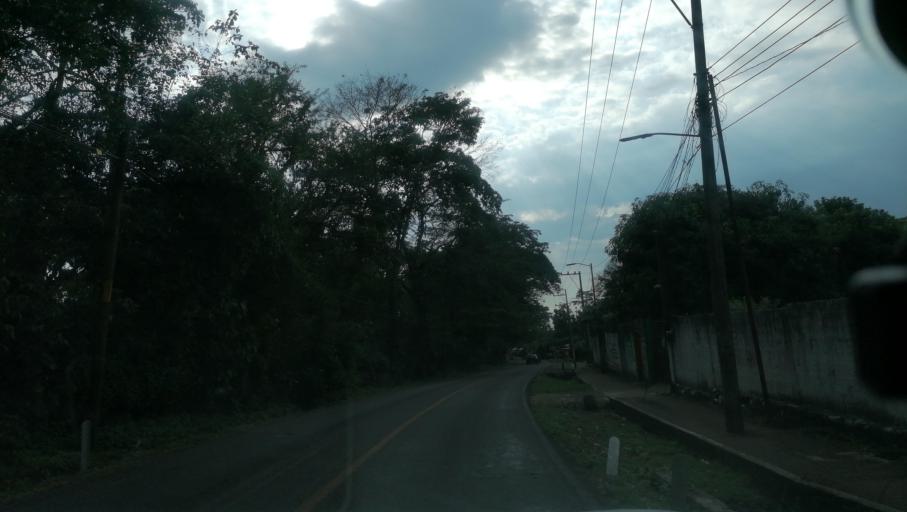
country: MX
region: Chiapas
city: Cacahoatan
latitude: 15.0029
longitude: -92.1588
